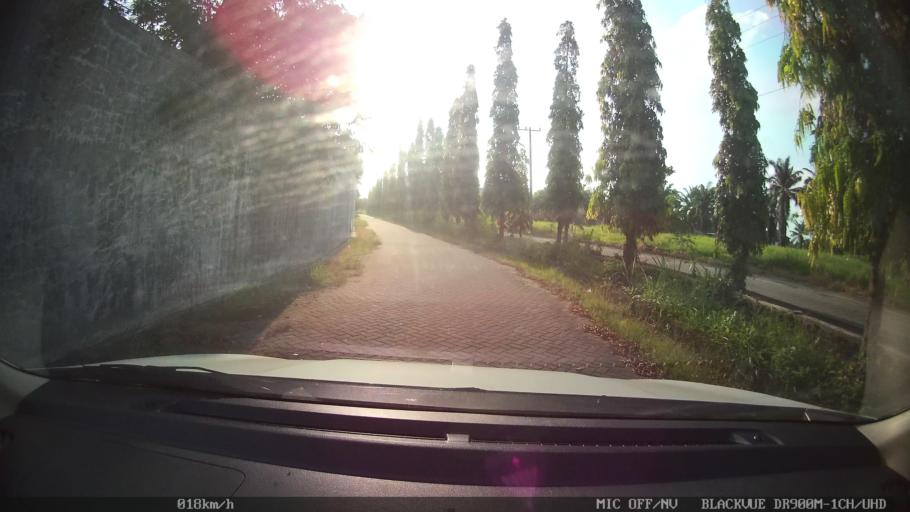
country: ID
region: North Sumatra
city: Medan
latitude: 3.6204
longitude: 98.6457
